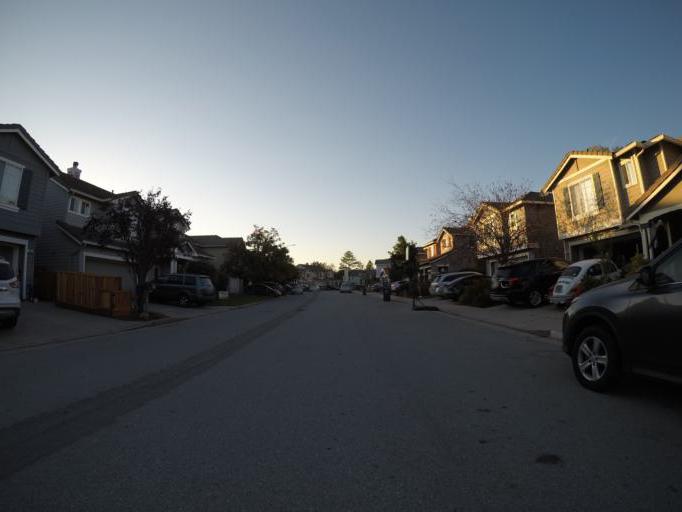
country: US
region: California
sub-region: Santa Cruz County
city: Scotts Valley
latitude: 37.0500
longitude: -122.0344
